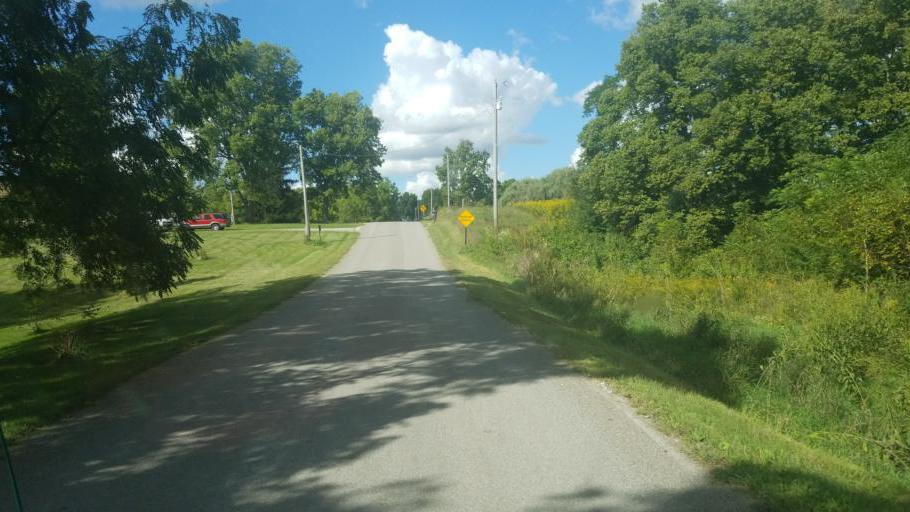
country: US
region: Ohio
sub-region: Hardin County
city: Kenton
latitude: 40.5407
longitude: -83.5435
